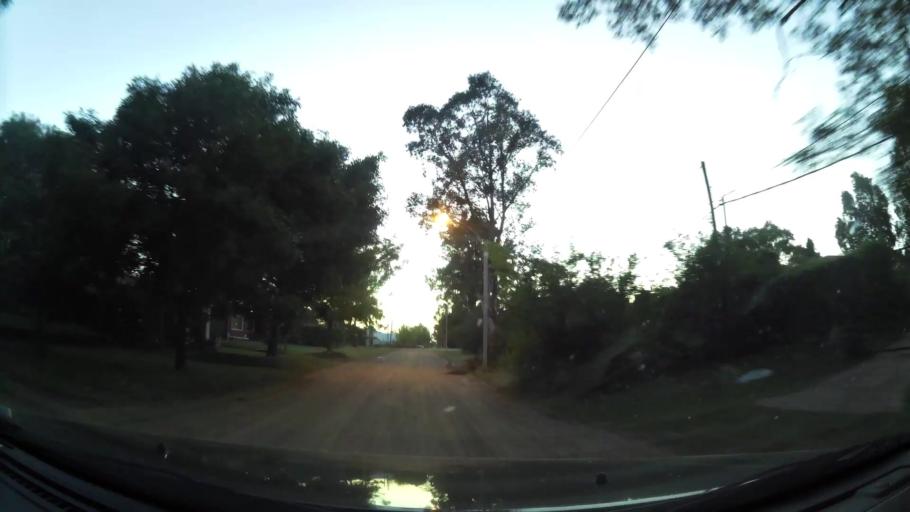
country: UY
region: Canelones
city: Atlantida
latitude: -34.7676
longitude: -55.7542
